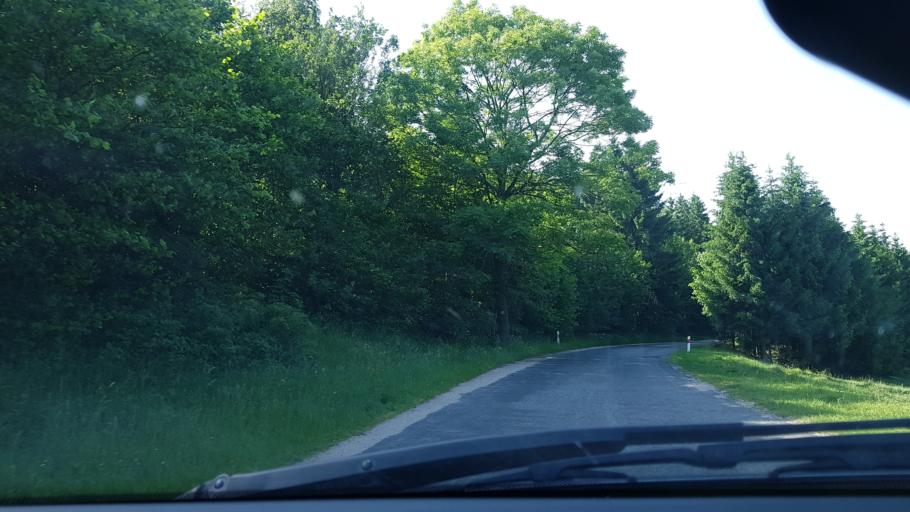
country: PL
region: Lower Silesian Voivodeship
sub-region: Powiat zabkowicki
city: Budzow
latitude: 50.5447
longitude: 16.6638
